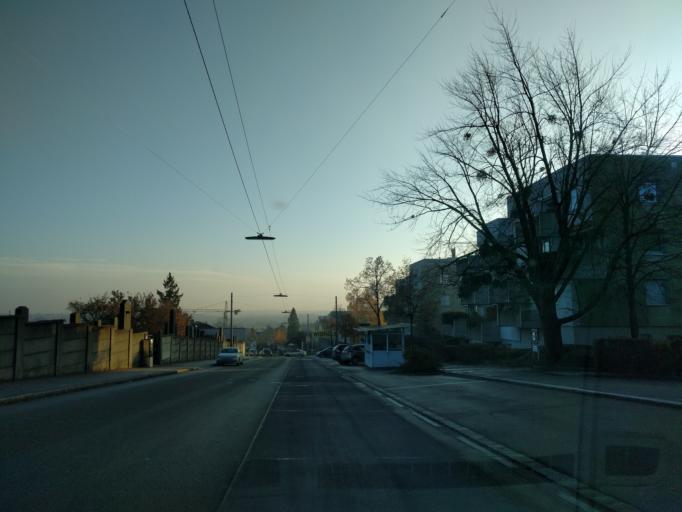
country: AT
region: Lower Austria
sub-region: Politischer Bezirk Modling
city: Perchtoldsdorf
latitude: 48.2026
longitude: 16.2789
